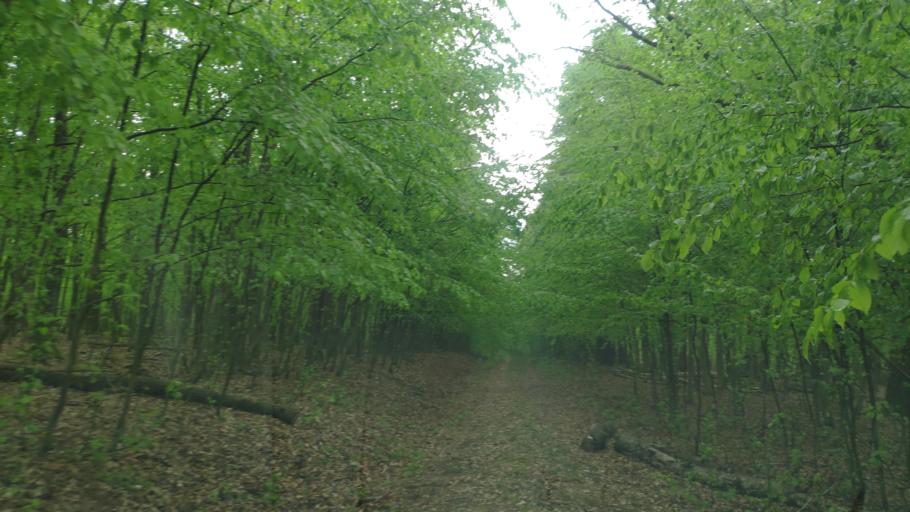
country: SK
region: Kosicky
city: Moldava nad Bodvou
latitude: 48.5474
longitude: 20.9304
